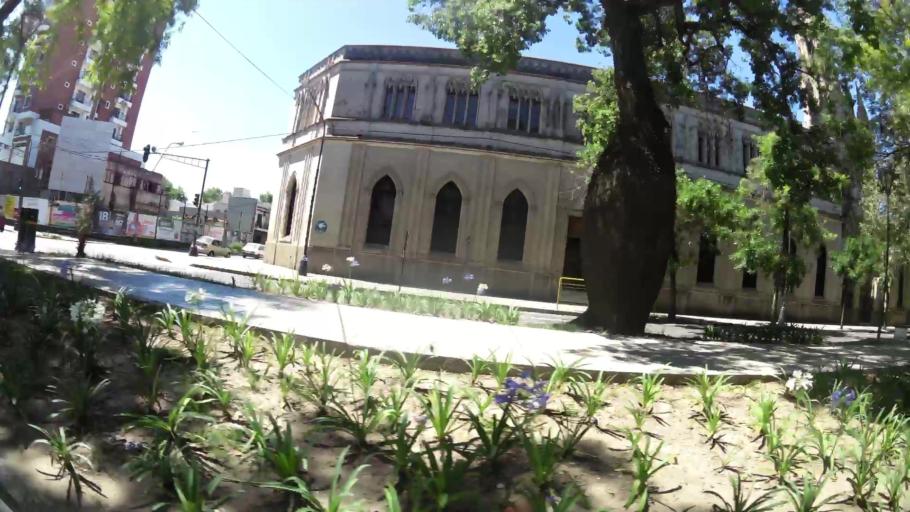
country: AR
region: Santa Fe
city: Santa Fe de la Vera Cruz
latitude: -31.6371
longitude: -60.6963
